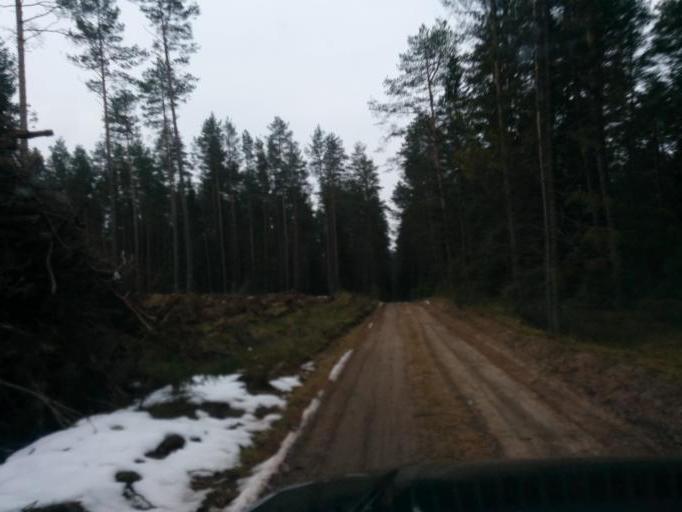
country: LV
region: Ikskile
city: Ikskile
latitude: 56.8036
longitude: 24.4834
